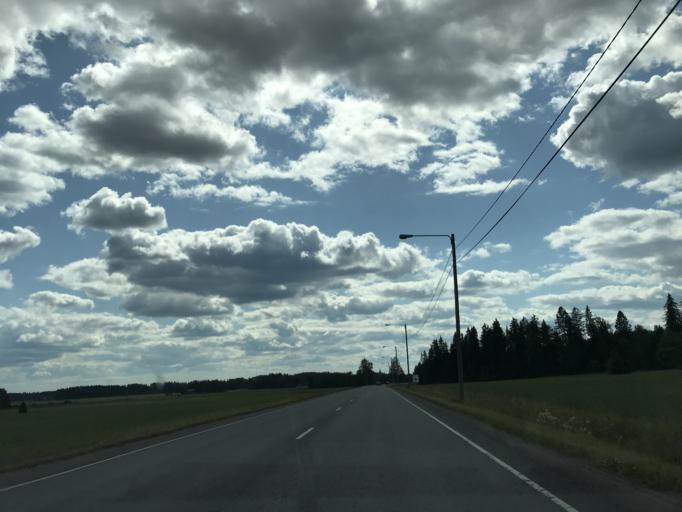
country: FI
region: Uusimaa
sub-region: Helsinki
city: Maentsaelae
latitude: 60.6563
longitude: 25.3443
